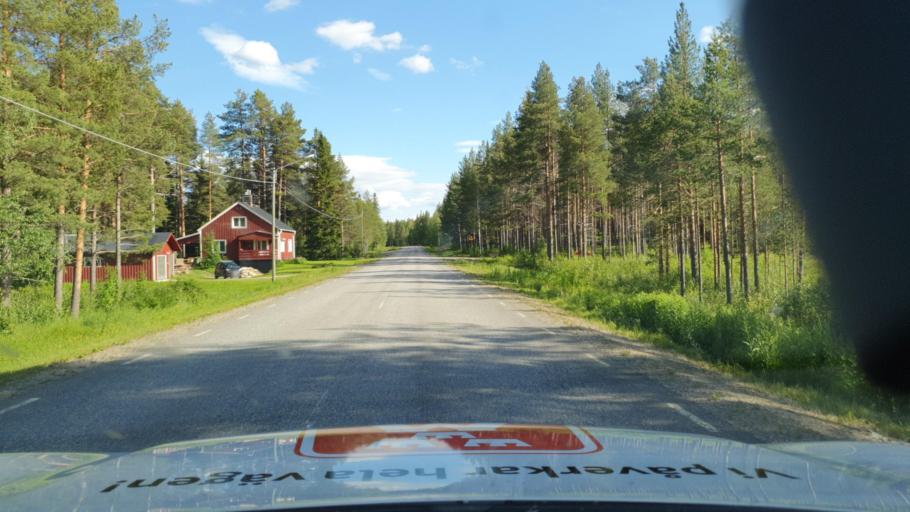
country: SE
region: Vaesterbotten
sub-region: Skelleftea Kommun
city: Langsele
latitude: 64.7999
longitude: 20.0104
